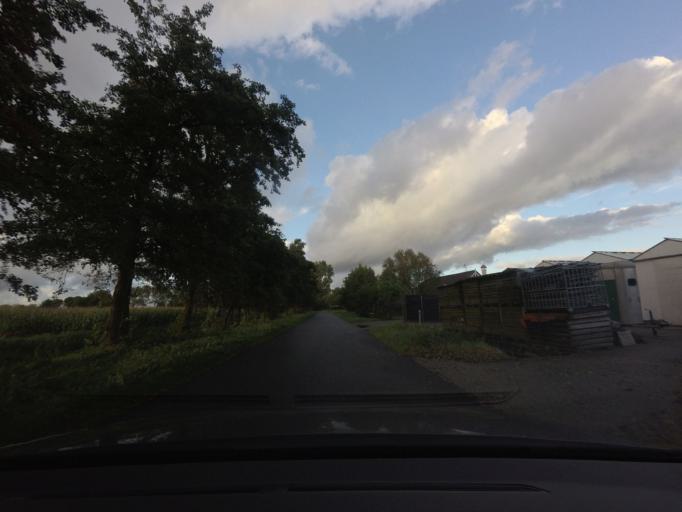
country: NL
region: North Holland
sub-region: Gemeente Langedijk
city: Broek op Langedijk
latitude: 52.6609
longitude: 4.7793
